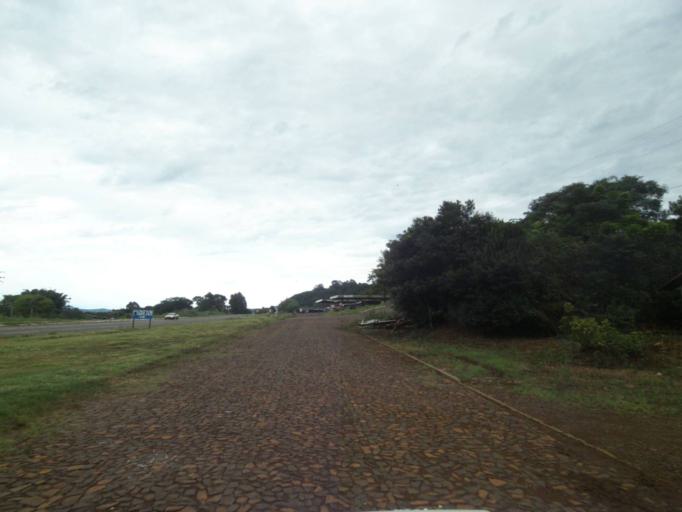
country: BR
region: Parana
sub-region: Guaraniacu
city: Guaraniacu
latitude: -25.1082
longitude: -52.8575
